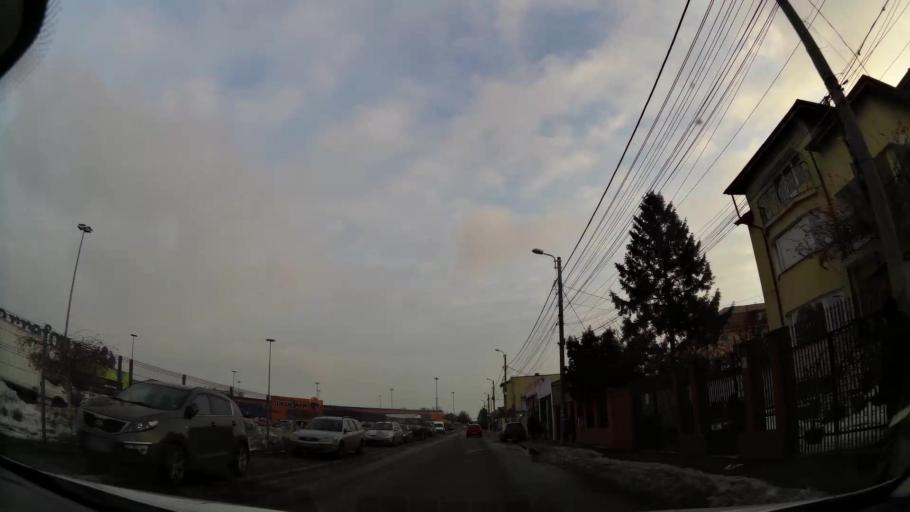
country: RO
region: Ilfov
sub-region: Comuna Fundeni-Dobroesti
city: Fundeni
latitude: 44.4746
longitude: 26.1598
